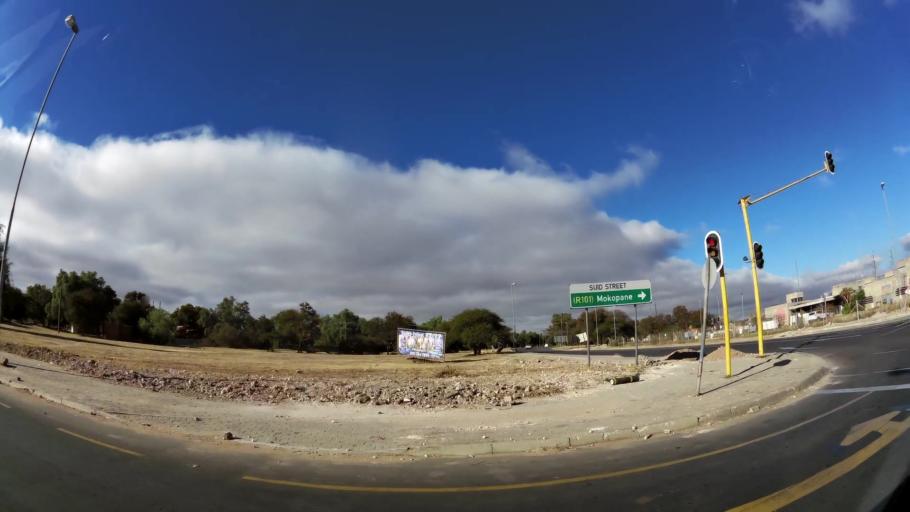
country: ZA
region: Limpopo
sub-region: Capricorn District Municipality
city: Polokwane
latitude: -23.9208
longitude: 29.4524
